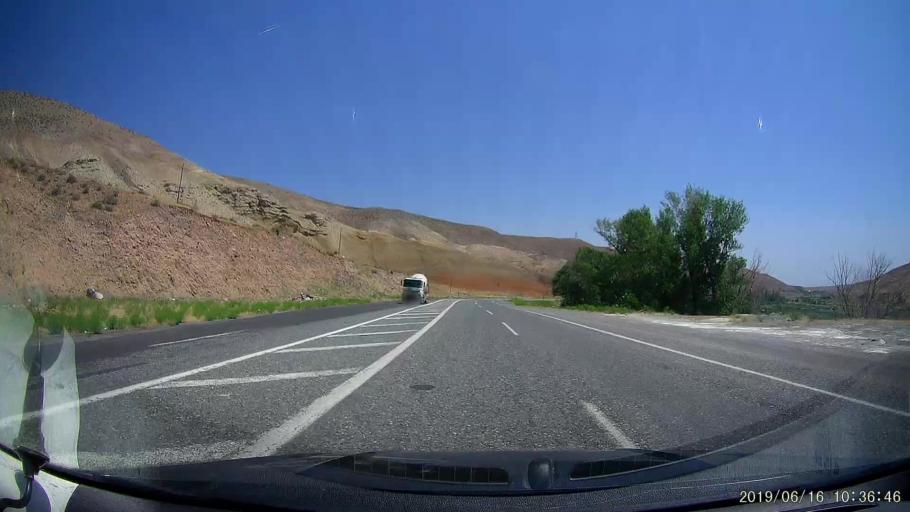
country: TR
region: Igdir
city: Tuzluca
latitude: 40.0416
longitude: 43.6865
